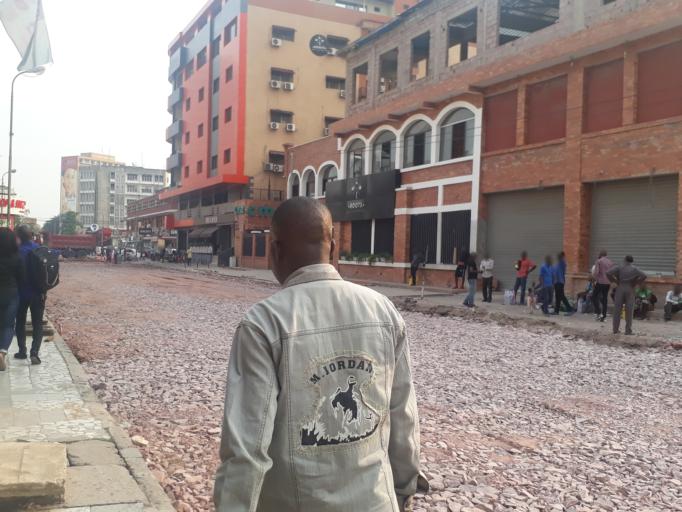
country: CD
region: Kinshasa
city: Kinshasa
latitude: -4.3009
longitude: 15.3109
